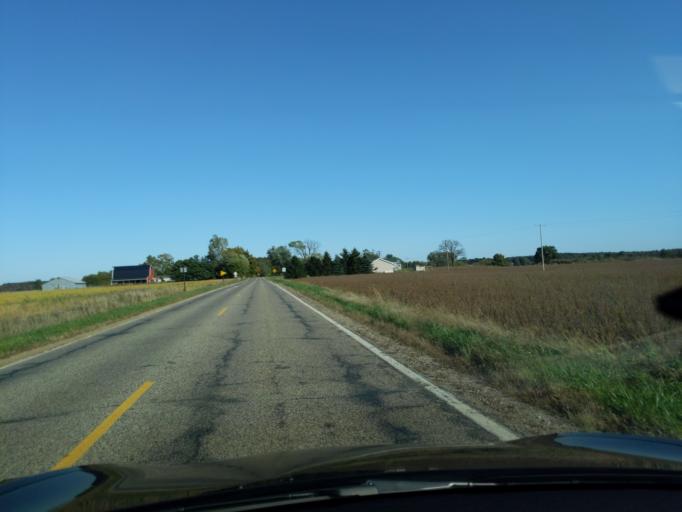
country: US
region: Michigan
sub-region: Clinton County
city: Saint Johns
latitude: 42.9289
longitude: -84.4829
